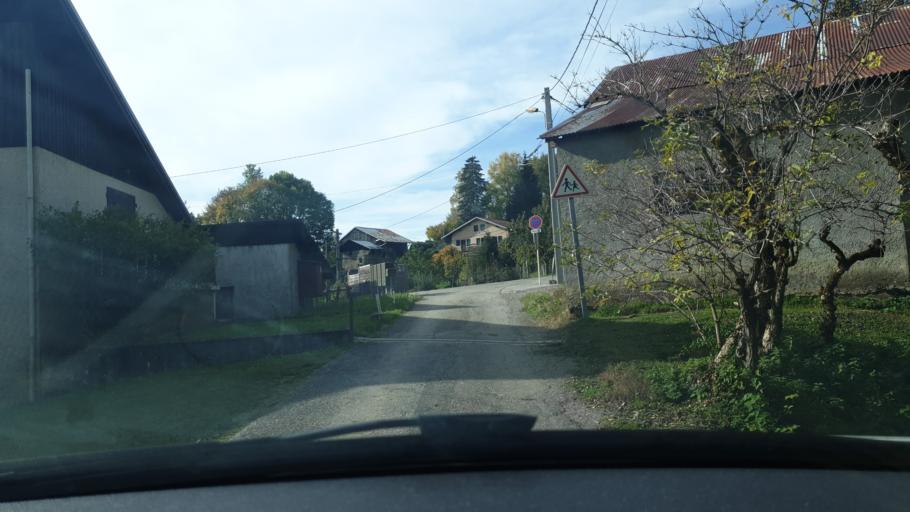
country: FR
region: Rhone-Alpes
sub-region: Departement de la Savoie
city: Aiton
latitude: 45.5032
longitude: 6.2304
